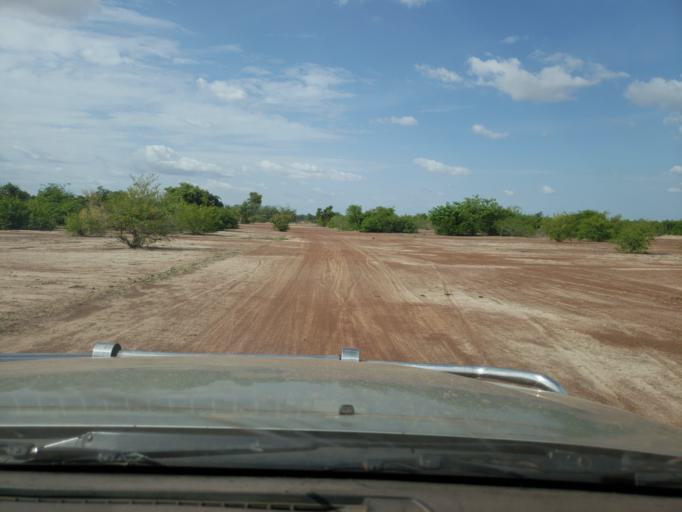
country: ML
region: Segou
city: Bla
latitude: 12.7856
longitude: -5.6063
